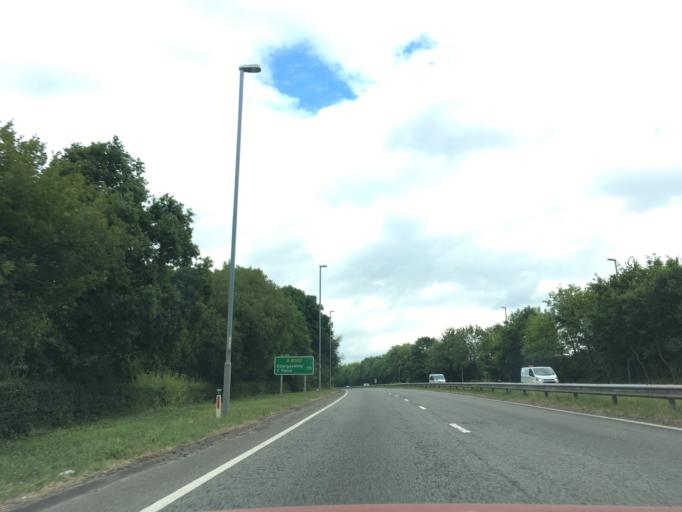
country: GB
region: Wales
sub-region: Torfaen County Borough
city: Cwmbran
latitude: 51.6518
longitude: -3.0003
